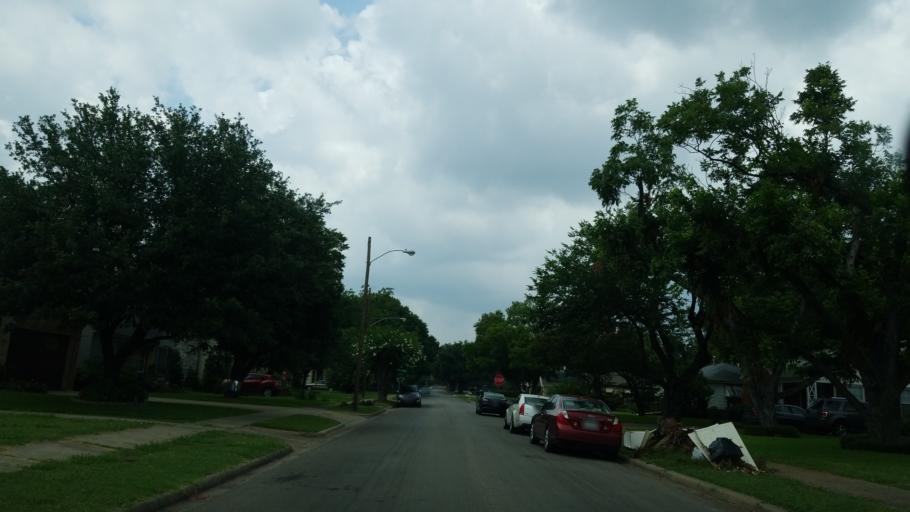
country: US
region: Texas
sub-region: Dallas County
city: University Park
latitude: 32.8461
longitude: -96.8227
